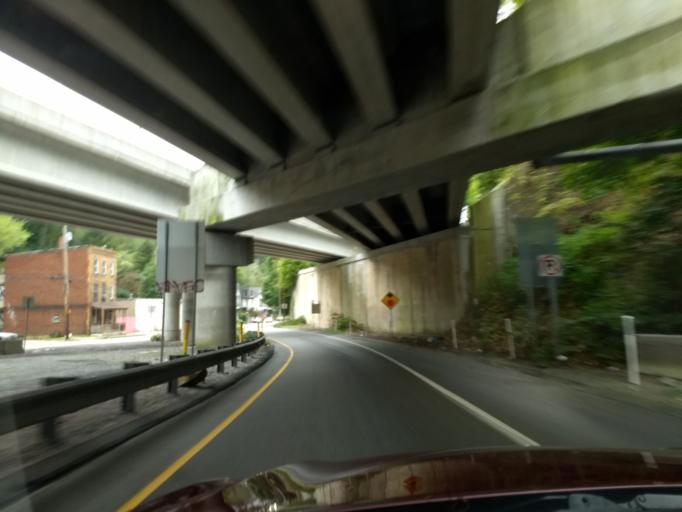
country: US
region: Pennsylvania
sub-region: Allegheny County
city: North Braddock
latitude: 40.4064
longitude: -79.8407
